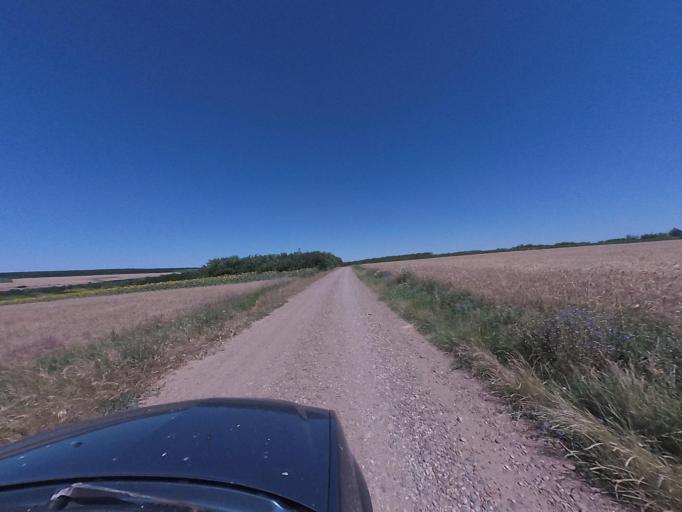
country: RO
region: Vaslui
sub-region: Comuna Costesti
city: Costesti
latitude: 46.4822
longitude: 27.7743
